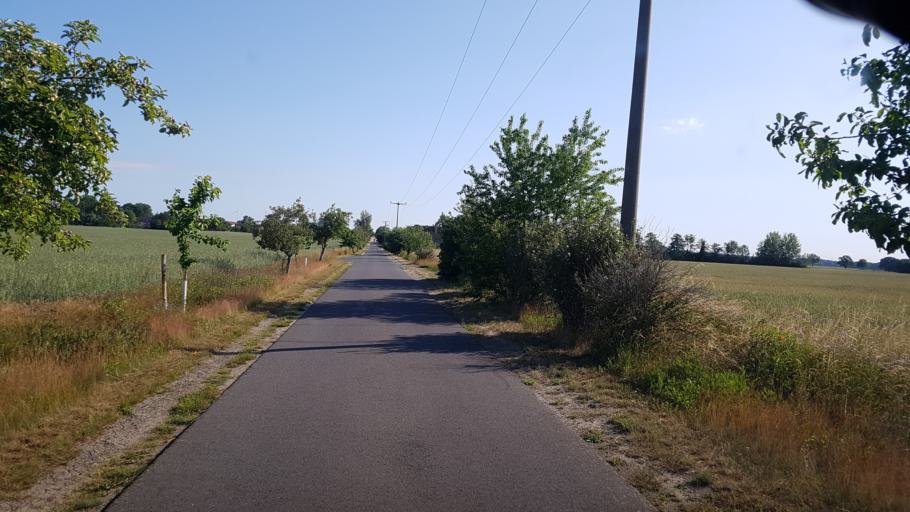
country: DE
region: Brandenburg
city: Sallgast
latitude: 51.6012
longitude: 13.8606
